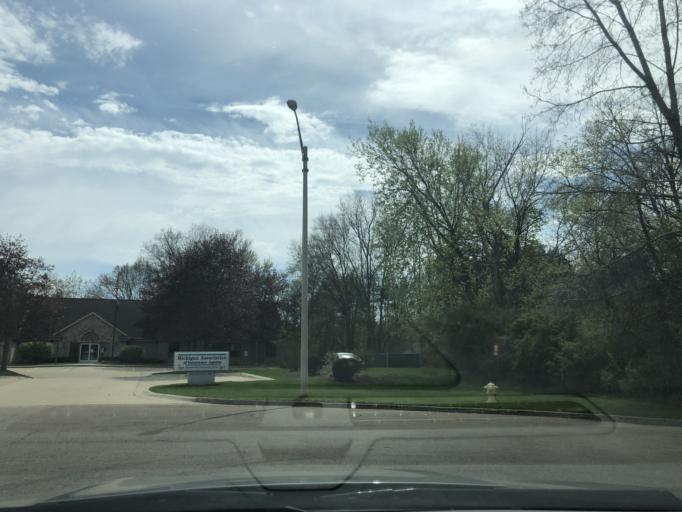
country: US
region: Michigan
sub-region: Eaton County
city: Waverly
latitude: 42.7213
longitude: -84.6466
